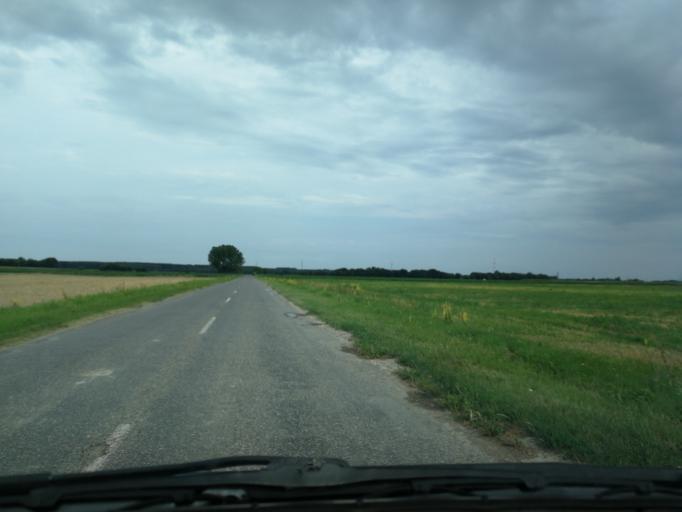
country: HU
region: Bacs-Kiskun
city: Batya
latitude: 46.4524
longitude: 18.9625
